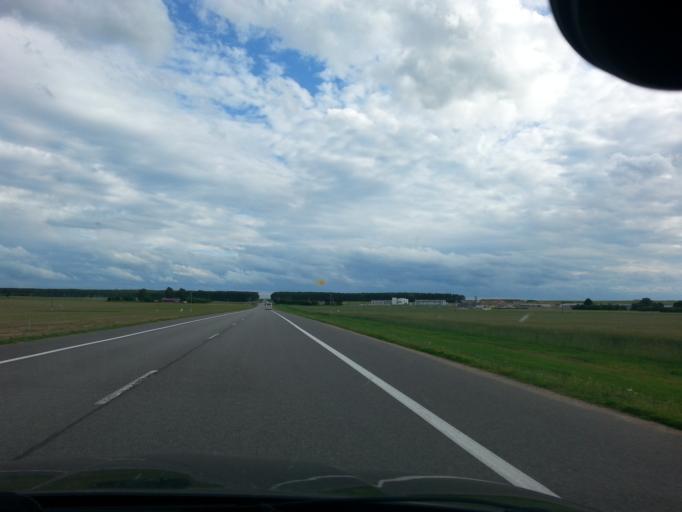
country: BY
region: Grodnenskaya
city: Astravyets
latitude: 54.7191
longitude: 26.0835
